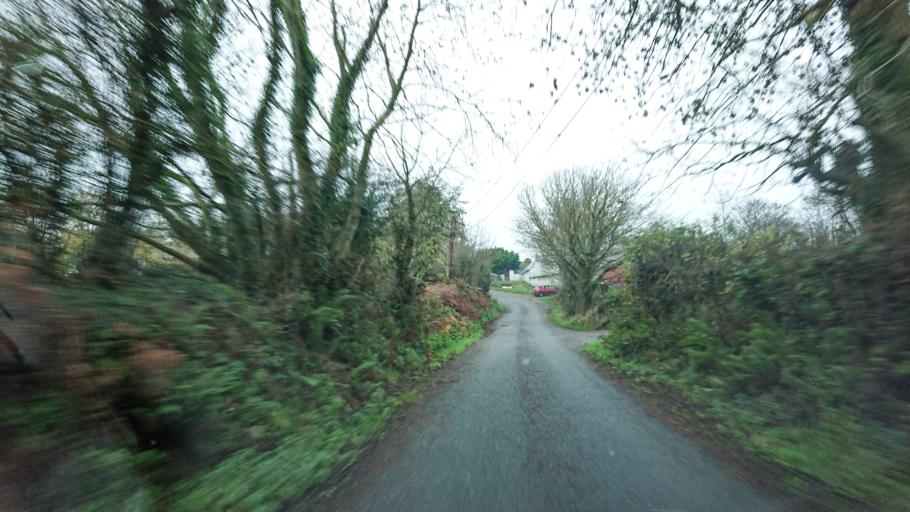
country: IE
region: Munster
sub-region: Waterford
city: Tra Mhor
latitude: 52.1998
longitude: -7.1598
